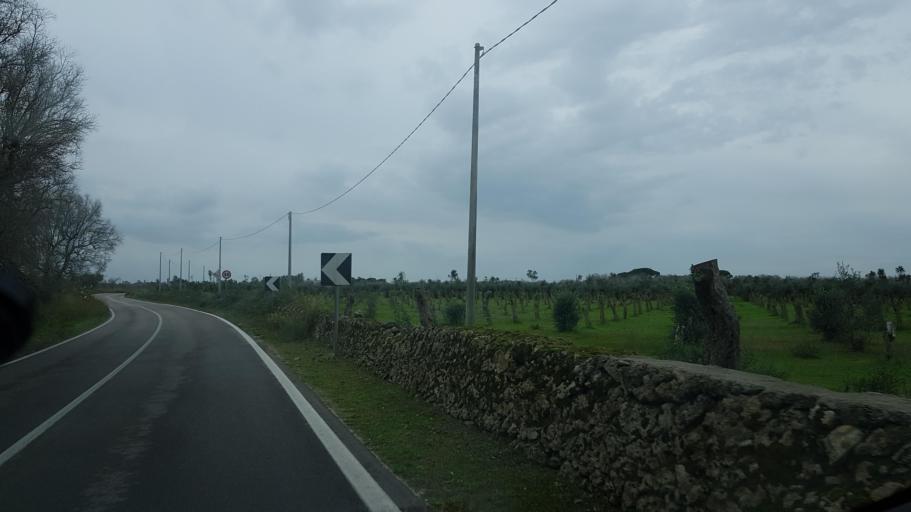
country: IT
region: Apulia
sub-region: Provincia di Brindisi
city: Torchiarolo
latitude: 40.4579
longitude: 18.0543
